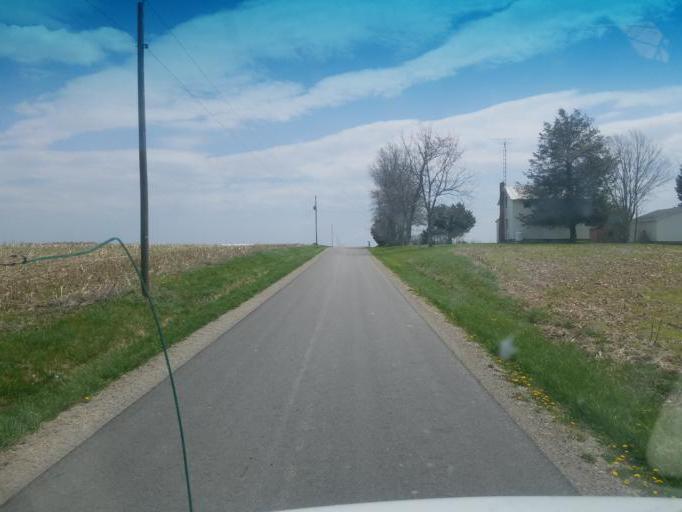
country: US
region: Ohio
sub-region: Hardin County
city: Forest
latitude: 40.7737
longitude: -83.4088
